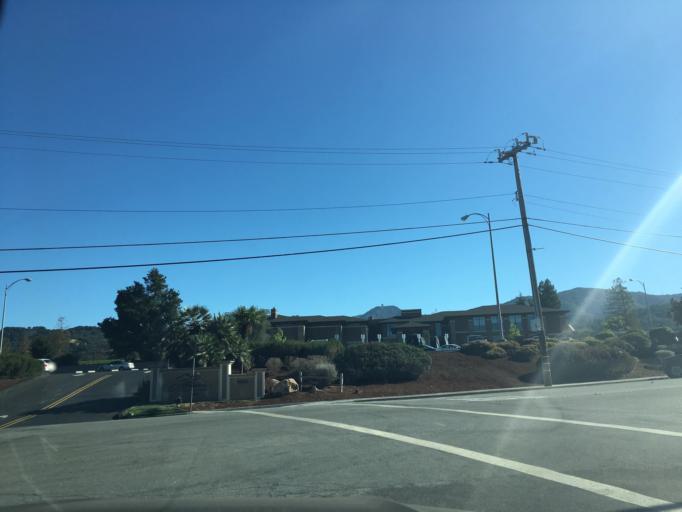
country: US
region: California
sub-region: Santa Clara County
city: Seven Trees
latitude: 37.2150
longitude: -121.8657
